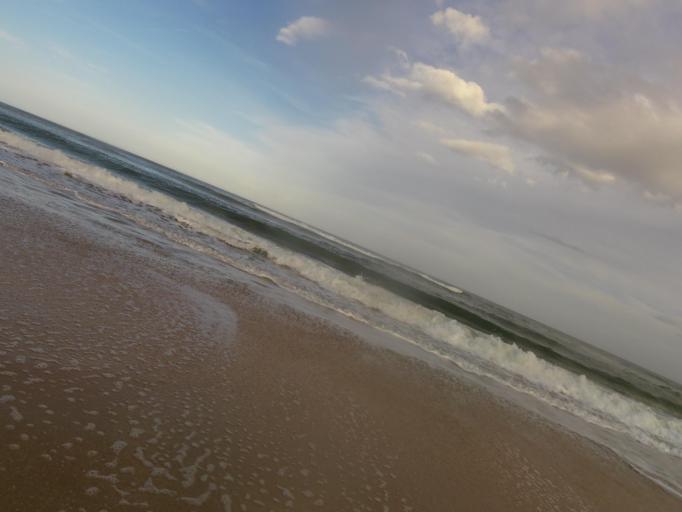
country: US
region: Florida
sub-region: Flagler County
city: Palm Coast
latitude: 29.6275
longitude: -81.1952
